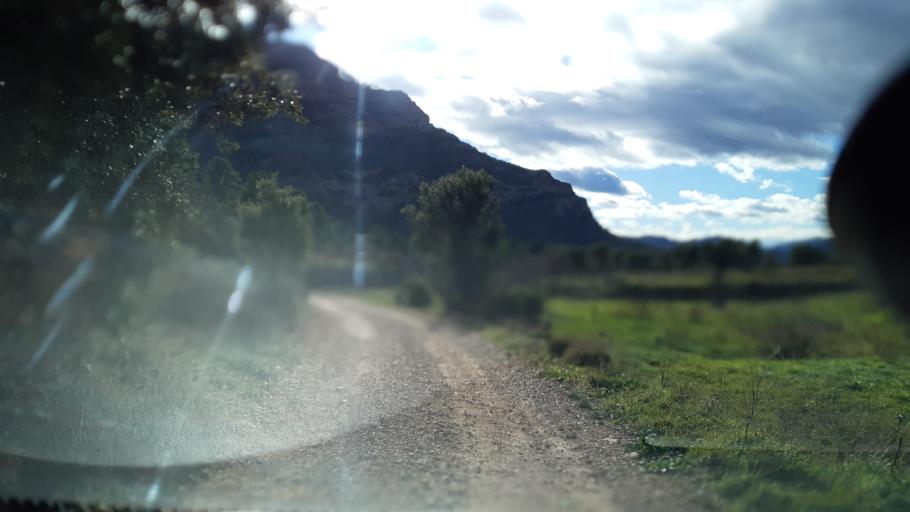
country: ES
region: Aragon
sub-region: Provincia de Teruel
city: Valderrobres
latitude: 40.8564
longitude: 0.2324
